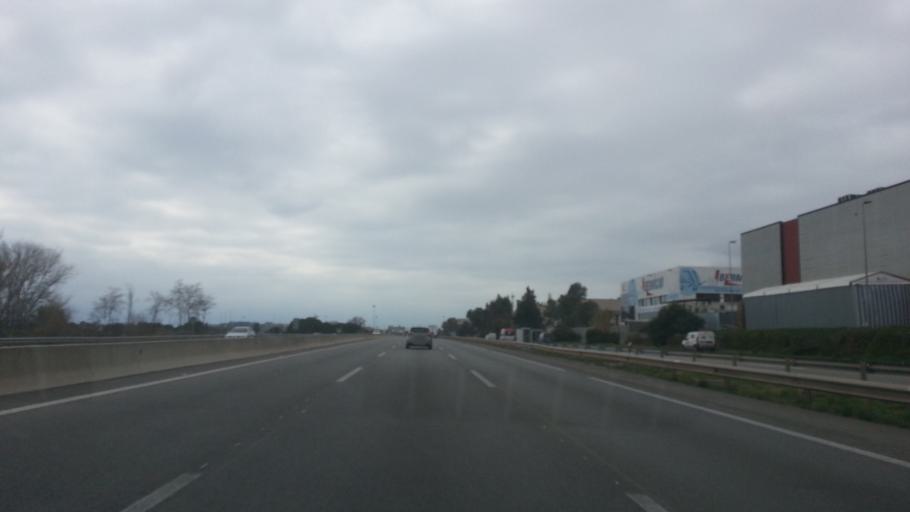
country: ES
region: Catalonia
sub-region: Provincia de Barcelona
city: Gava
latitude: 41.2856
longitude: 1.9978
